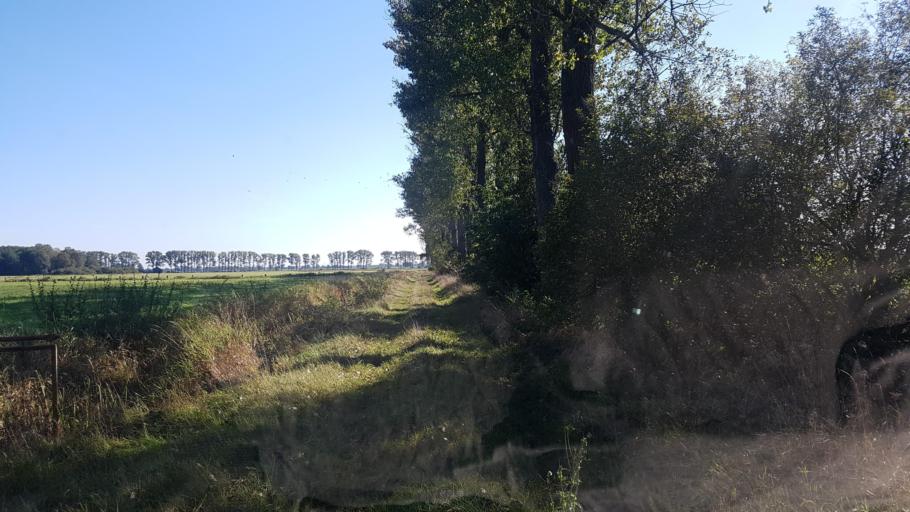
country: DE
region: Brandenburg
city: Hohenleipisch
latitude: 51.4644
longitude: 13.5718
